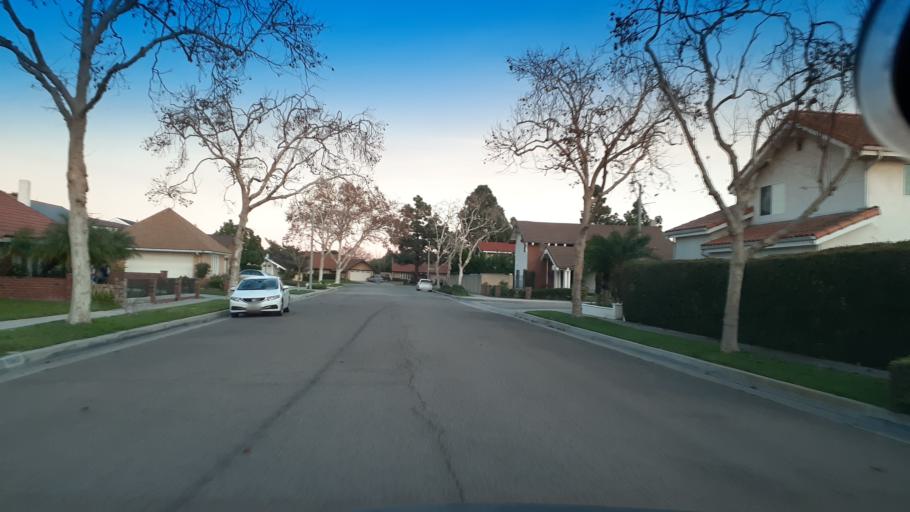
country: US
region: California
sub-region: Los Angeles County
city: Artesia
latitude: 33.8567
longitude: -118.0804
